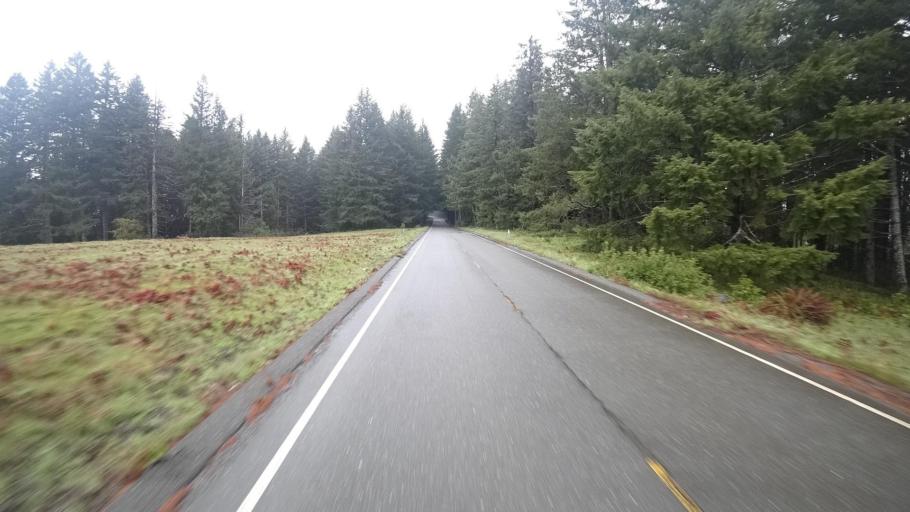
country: US
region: California
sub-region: Humboldt County
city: Westhaven-Moonstone
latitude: 41.1956
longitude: -123.9421
